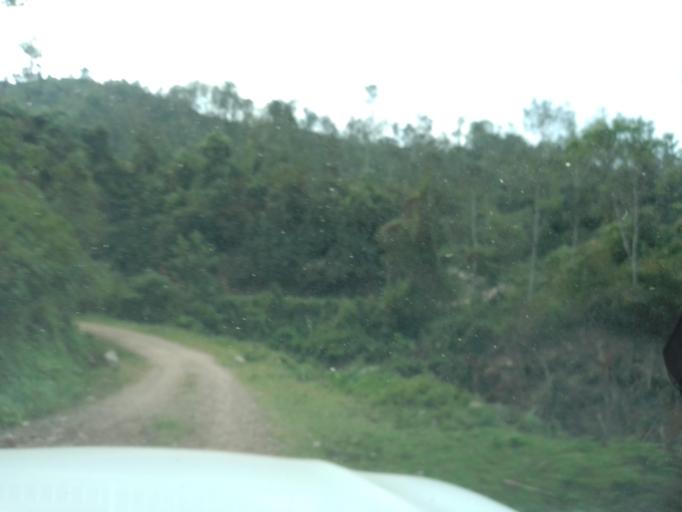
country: MX
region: Chiapas
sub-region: Cacahoatan
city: Benito Juarez
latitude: 15.2073
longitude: -92.2205
